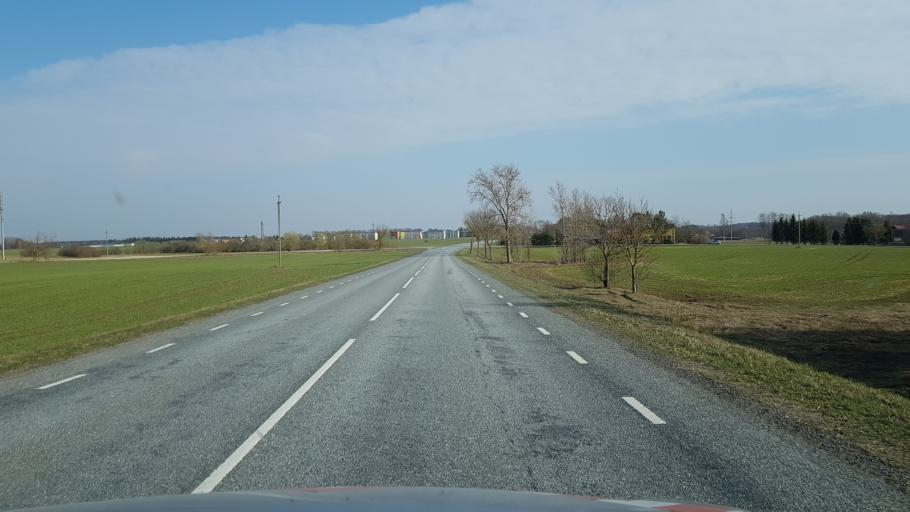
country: EE
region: Laeaene-Virumaa
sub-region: Kadrina vald
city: Kadrina
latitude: 59.3550
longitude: 26.1163
